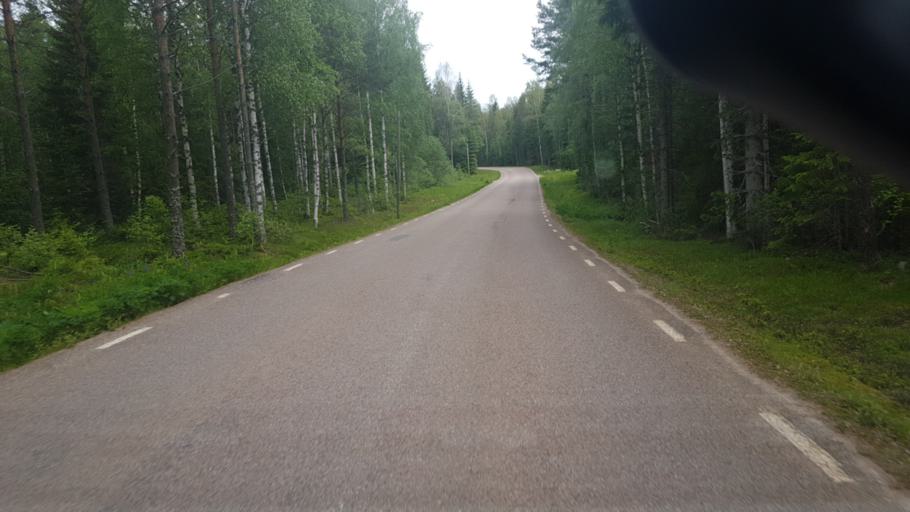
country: SE
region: Vaermland
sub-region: Arvika Kommun
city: Arvika
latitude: 59.7878
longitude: 12.8386
